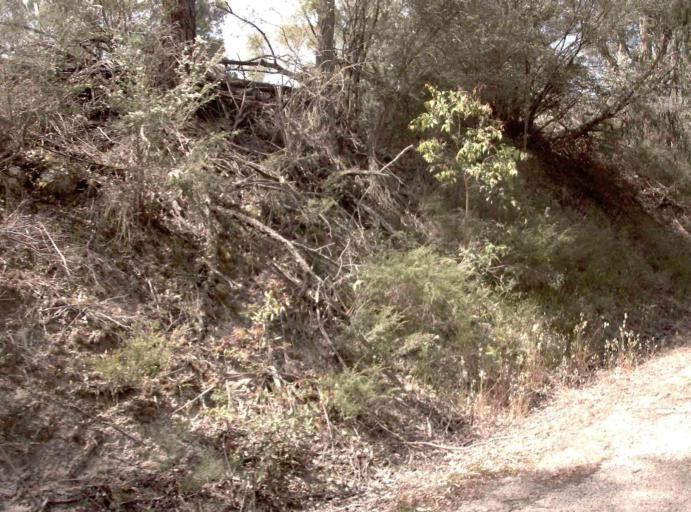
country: AU
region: New South Wales
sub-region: Bega Valley
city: Eden
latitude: -37.4815
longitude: 149.6304
